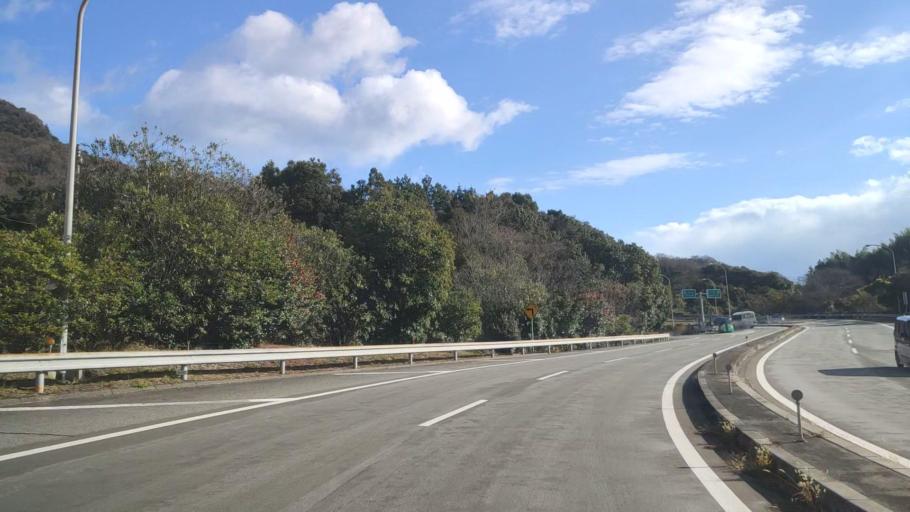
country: JP
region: Hiroshima
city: Innoshima
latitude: 34.2052
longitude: 133.0768
